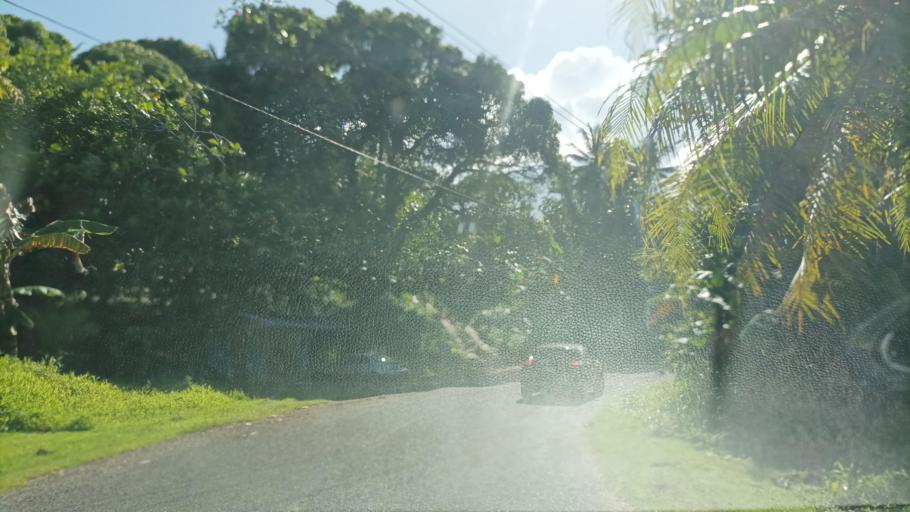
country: FM
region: Pohnpei
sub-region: Madolenihm Municipality
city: Madolenihm Municipality Government
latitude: 6.9130
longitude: 158.2986
